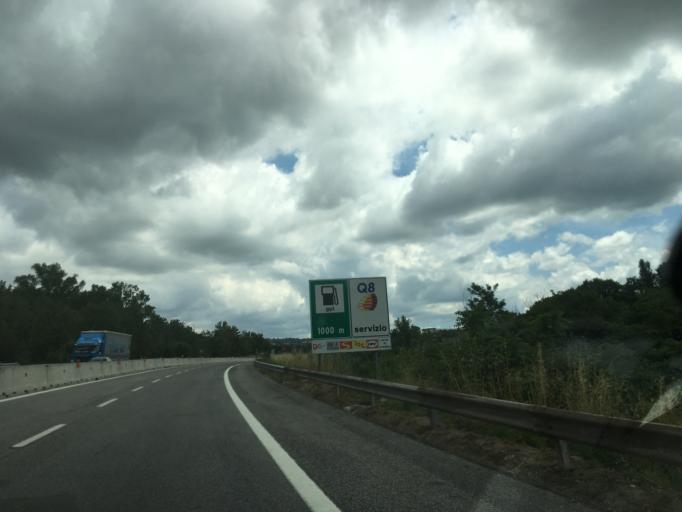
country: IT
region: Campania
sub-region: Provincia di Avellino
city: Passo di Mirabella-Pianopantano
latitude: 41.0676
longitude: 15.0055
